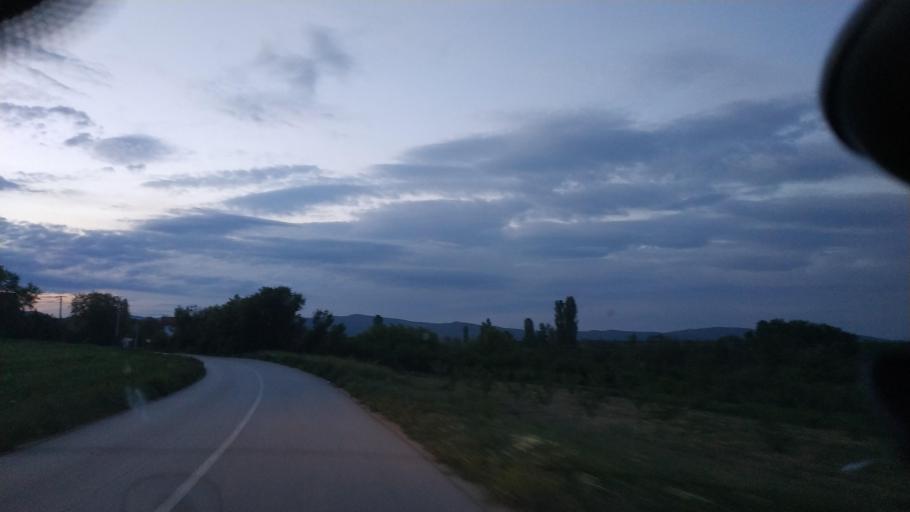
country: RS
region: Central Serbia
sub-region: Nisavski Okrug
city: Merosina
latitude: 43.3028
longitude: 21.6944
